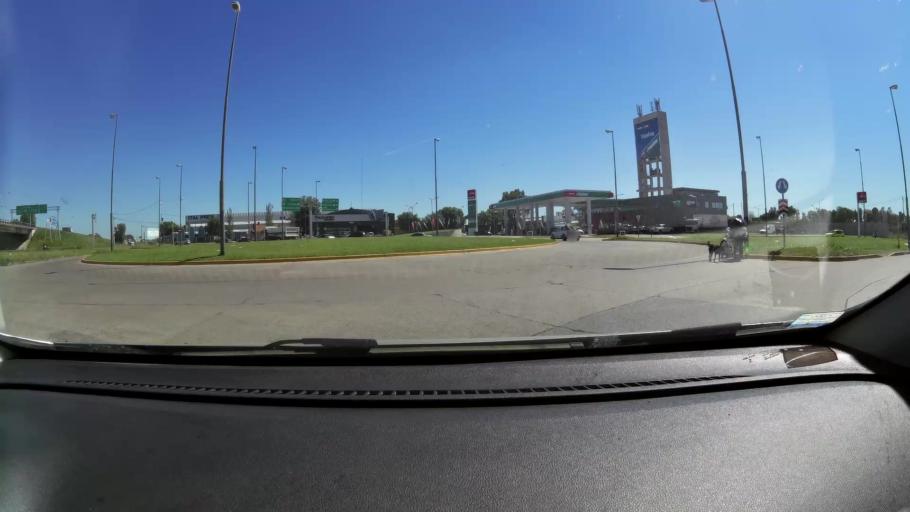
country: AR
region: Santa Fe
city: Perez
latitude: -32.9711
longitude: -60.7159
